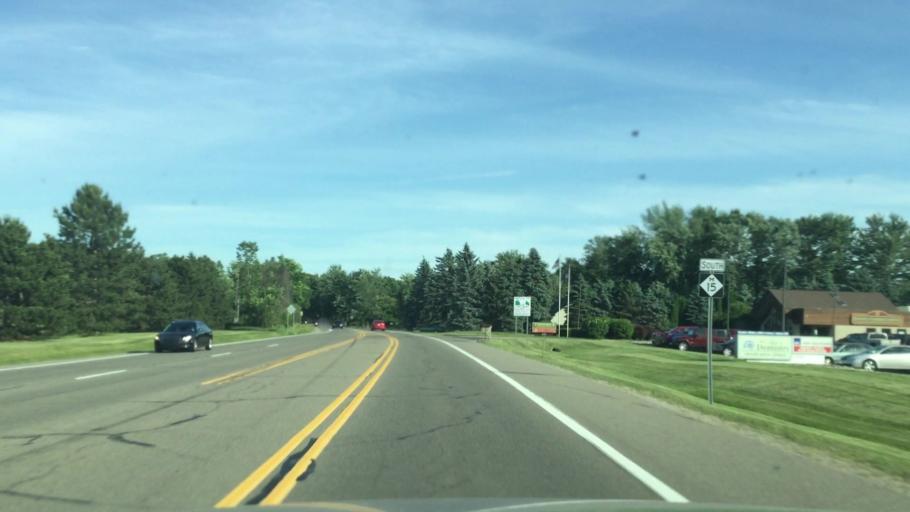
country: US
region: Michigan
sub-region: Genesee County
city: Davison
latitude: 43.0049
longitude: -83.5156
